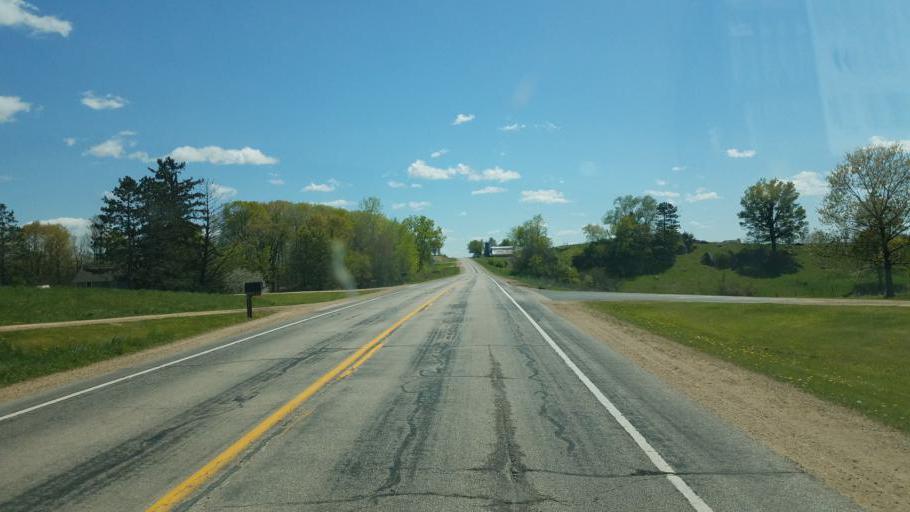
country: US
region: Wisconsin
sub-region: Vernon County
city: Hillsboro
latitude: 43.5940
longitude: -90.3521
